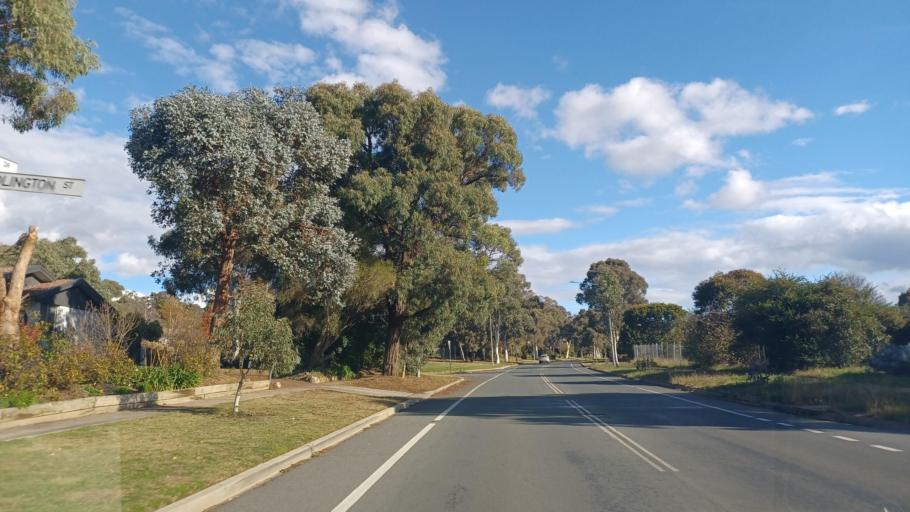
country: AU
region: Australian Capital Territory
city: Belconnen
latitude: -35.1892
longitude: 149.0471
